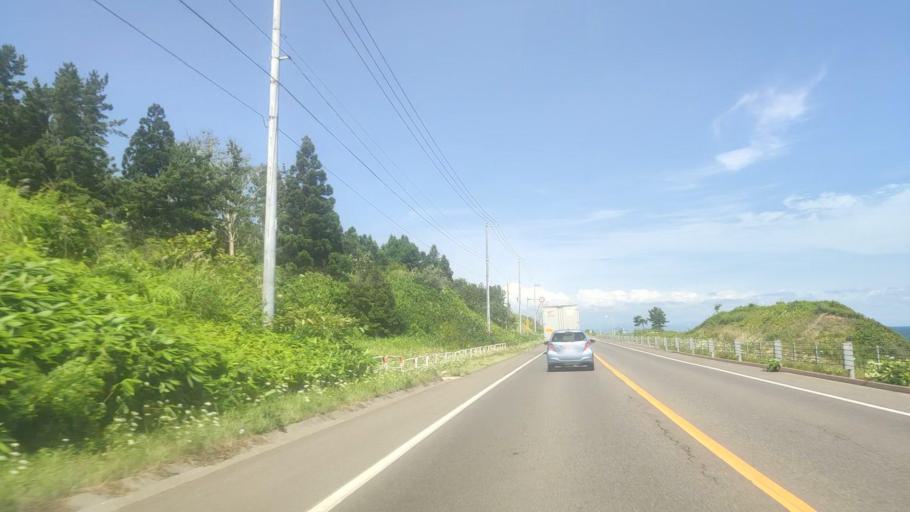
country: JP
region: Hokkaido
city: Nanae
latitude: 42.2022
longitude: 140.4073
